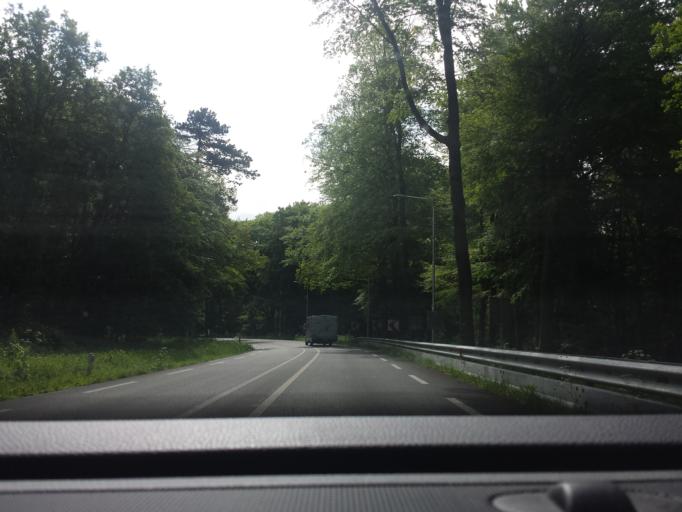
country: NL
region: Gelderland
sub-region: Gemeente Lochem
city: Barchem
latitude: 52.0832
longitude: 6.4193
